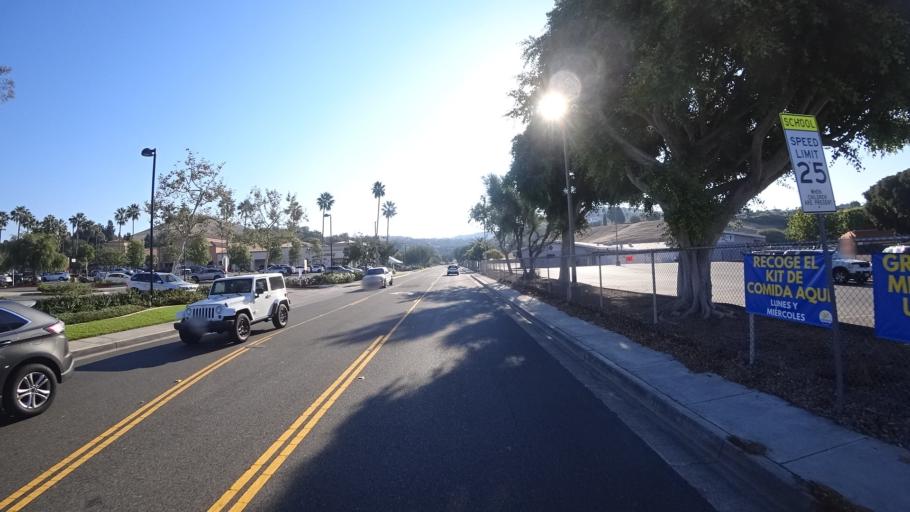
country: US
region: California
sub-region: Orange County
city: San Clemente
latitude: 33.4422
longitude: -117.6153
